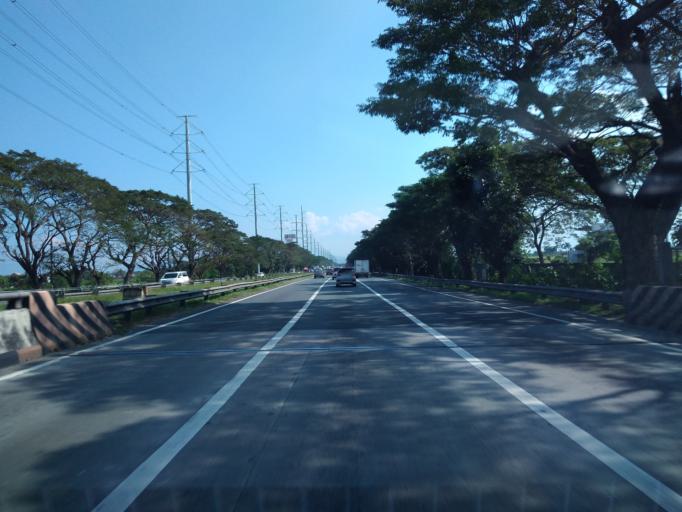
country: PH
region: Calabarzon
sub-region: Province of Laguna
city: Pulong Santa Cruz
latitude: 14.2711
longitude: 121.0955
